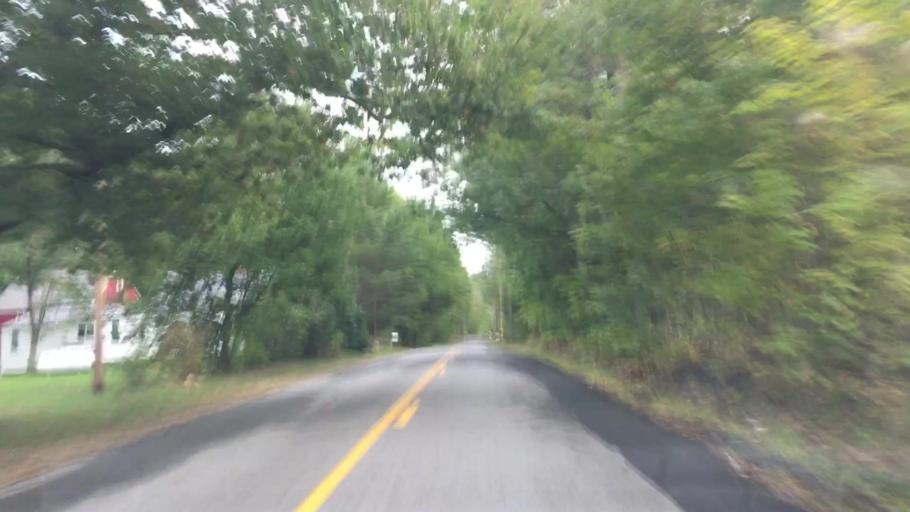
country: US
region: Maine
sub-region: York County
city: Parsonsfield
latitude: 43.6987
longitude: -70.9812
